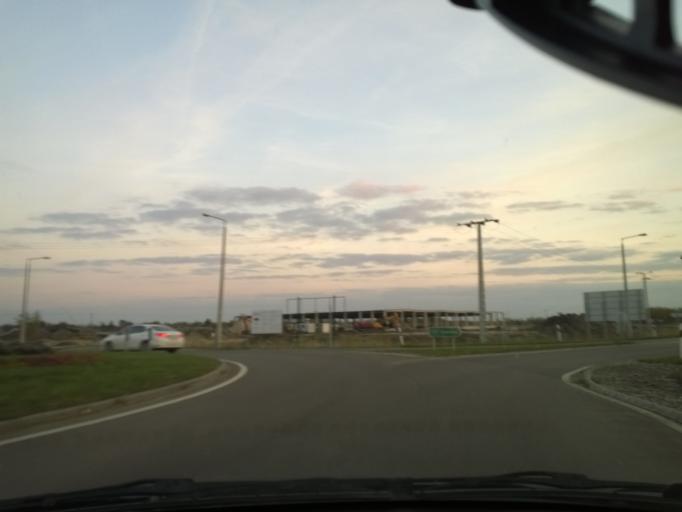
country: HU
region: Csongrad
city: Csongrad
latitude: 46.7171
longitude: 20.1142
